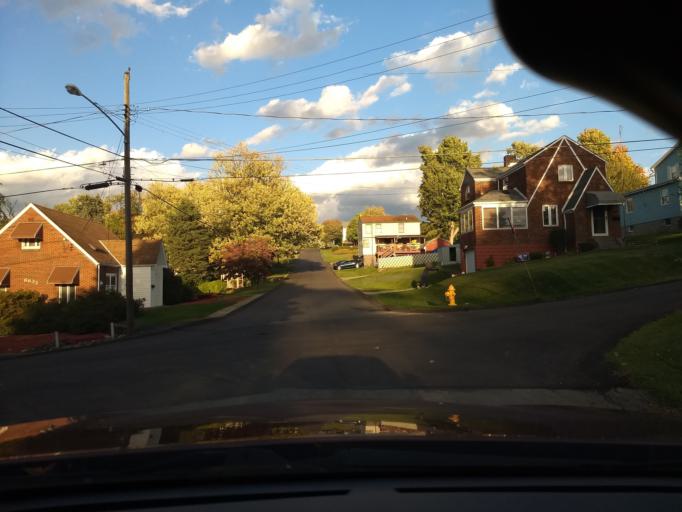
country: US
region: Pennsylvania
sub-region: Allegheny County
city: Dravosburg
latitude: 40.3535
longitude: -79.9058
